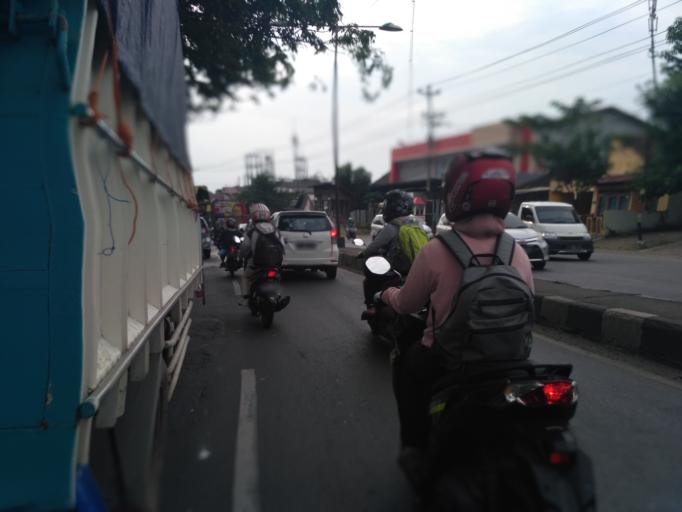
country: ID
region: Central Java
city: Semarang
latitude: -6.9849
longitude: 110.3571
